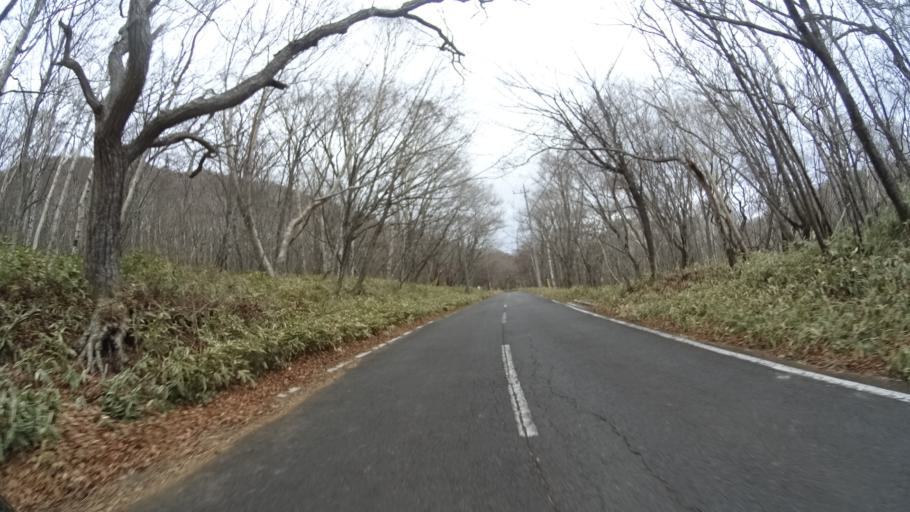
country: JP
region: Gunma
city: Omamacho-omama
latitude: 36.5341
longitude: 139.1764
